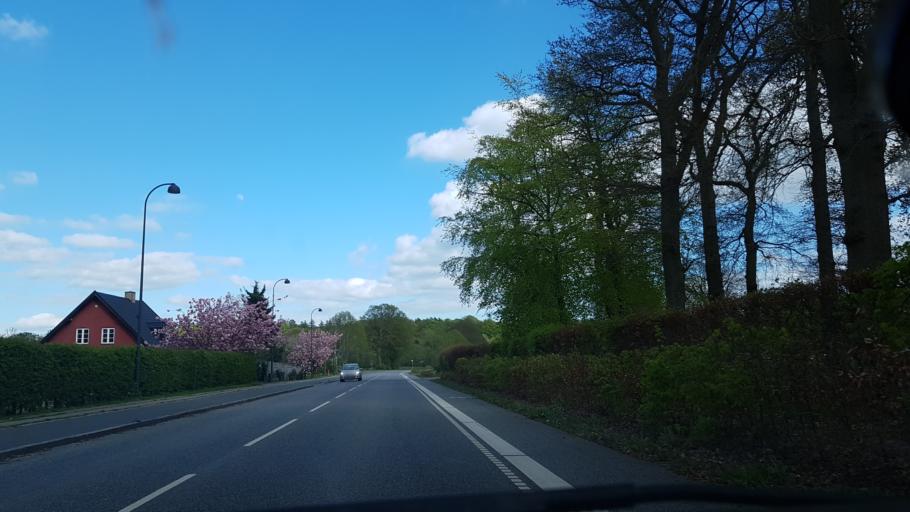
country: DK
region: Capital Region
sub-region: Rudersdal Kommune
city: Trorod
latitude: 55.8282
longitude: 12.5355
